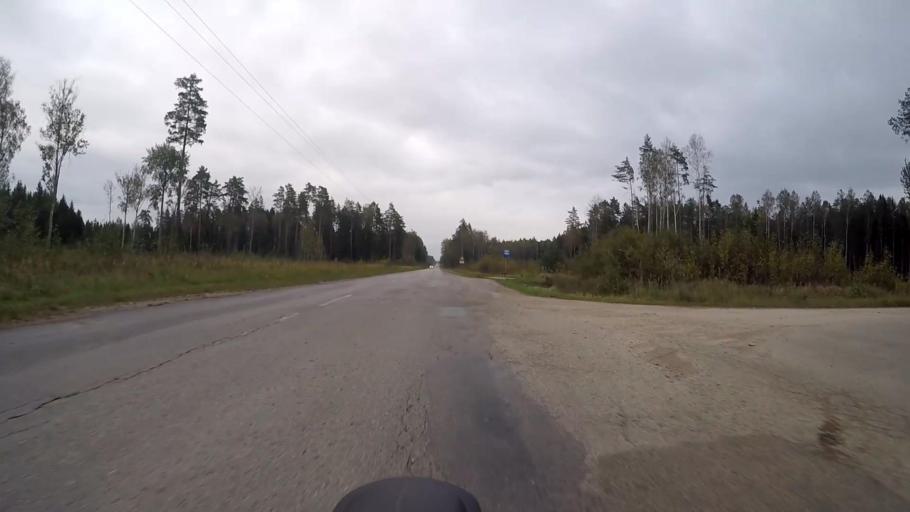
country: LV
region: Saulkrastu
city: Saulkrasti
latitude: 57.2716
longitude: 24.4875
